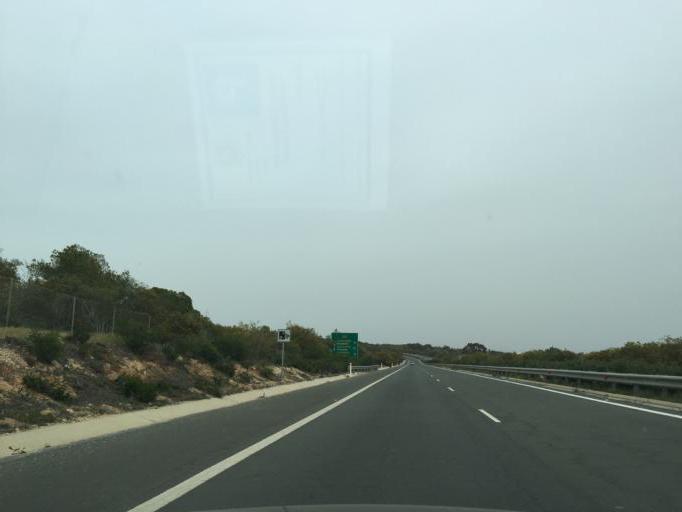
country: CY
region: Ammochostos
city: Ayia Napa
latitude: 34.9995
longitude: 33.9817
